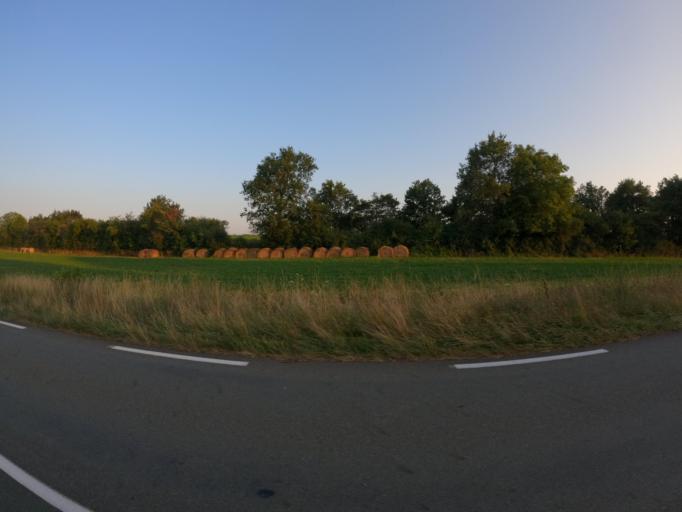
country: FR
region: Pays de la Loire
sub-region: Departement de Maine-et-Loire
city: Mire
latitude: 47.8701
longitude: -0.4678
